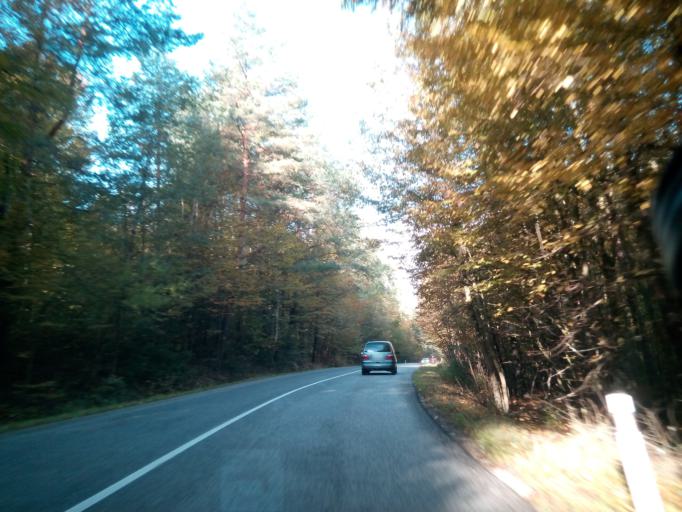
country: SK
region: Kosicky
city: Gelnica
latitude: 48.9093
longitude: 20.9591
